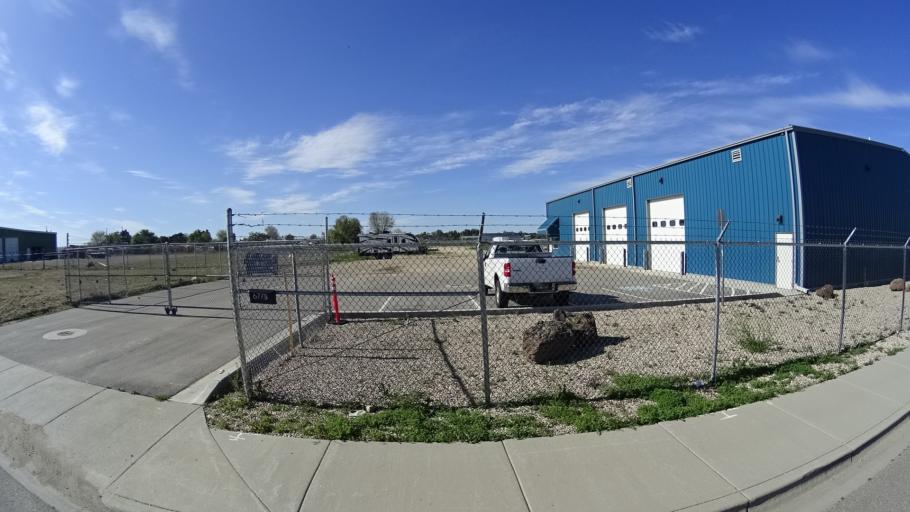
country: US
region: Idaho
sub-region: Ada County
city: Garden City
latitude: 43.5828
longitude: -116.2654
